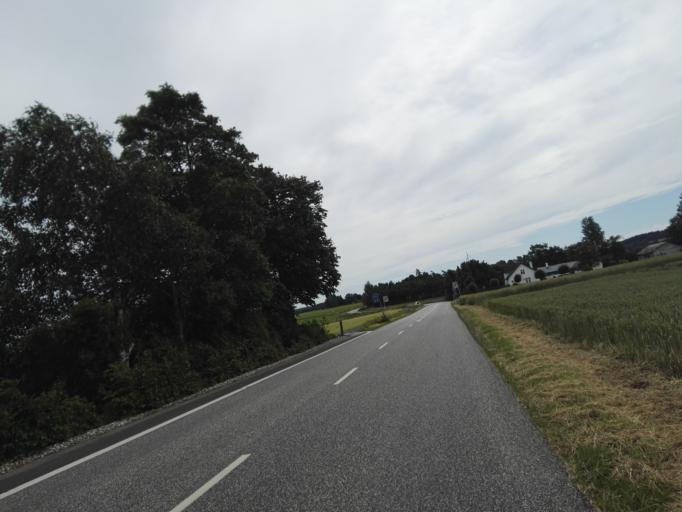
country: DK
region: Capital Region
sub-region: Hillerod Kommune
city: Skaevinge
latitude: 55.9016
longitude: 12.1513
